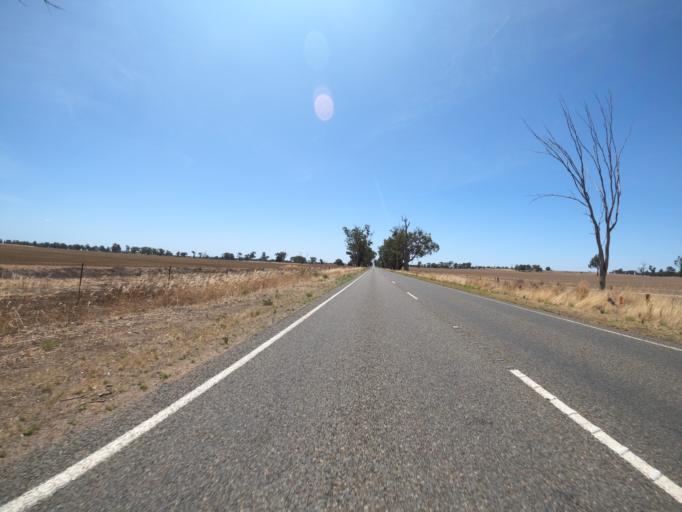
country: AU
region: Victoria
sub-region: Moira
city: Yarrawonga
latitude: -36.0620
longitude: 145.9955
